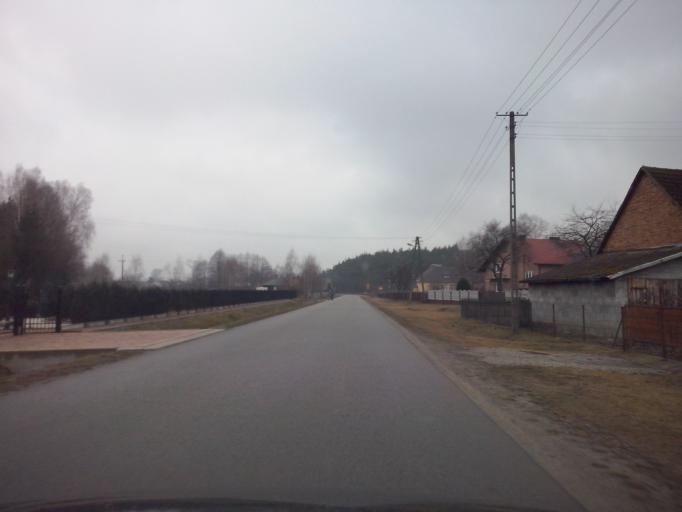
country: PL
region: Subcarpathian Voivodeship
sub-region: Powiat nizanski
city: Bieliny
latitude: 50.4439
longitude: 22.3008
